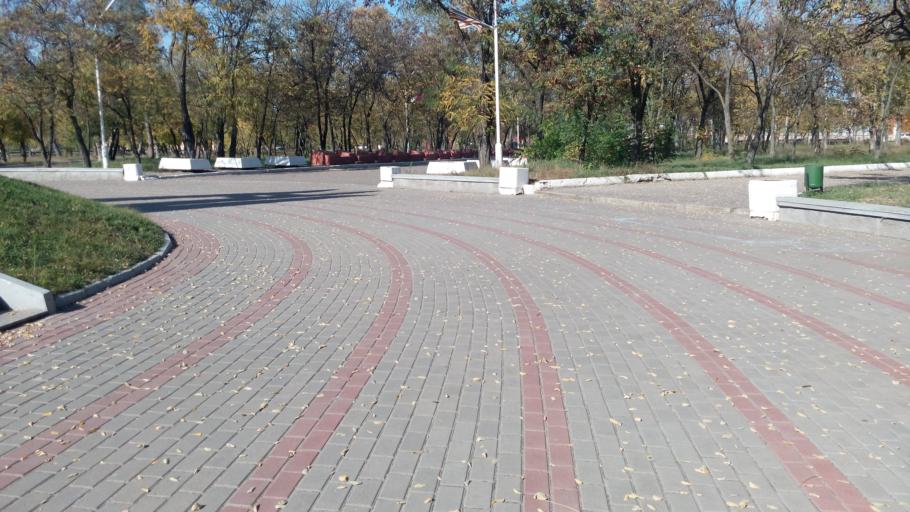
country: RU
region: Tambov
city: Kotovsk
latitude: 52.5915
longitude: 41.5045
